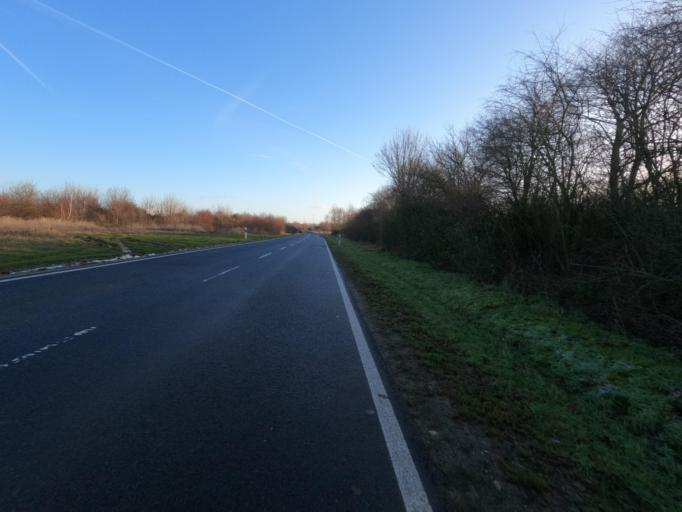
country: DE
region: North Rhine-Westphalia
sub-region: Regierungsbezirk Koln
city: Elsdorf
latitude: 50.9369
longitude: 6.5204
